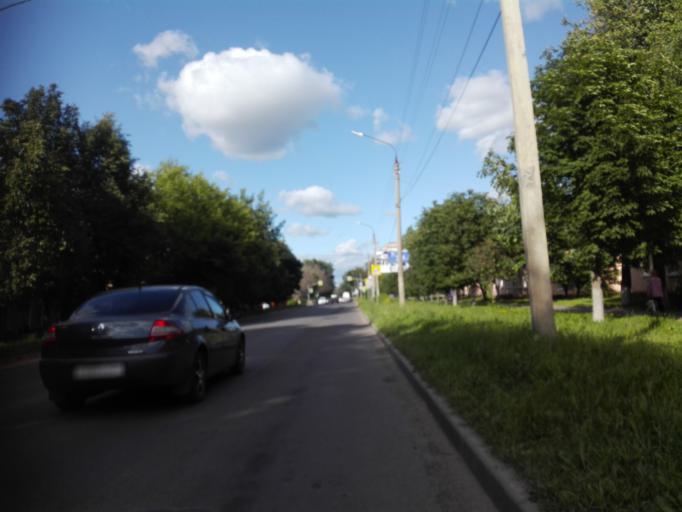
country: RU
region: Orjol
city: Orel
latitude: 52.9480
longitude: 36.0358
